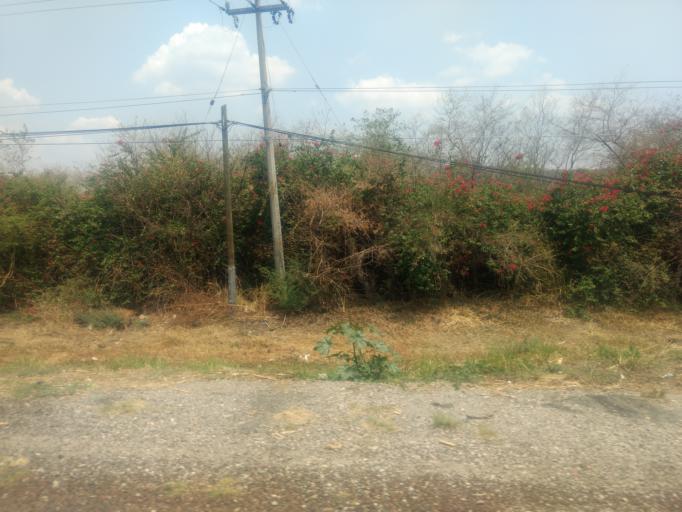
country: MX
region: Morelos
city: Puente de Ixtla
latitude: 18.6381
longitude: -99.3117
